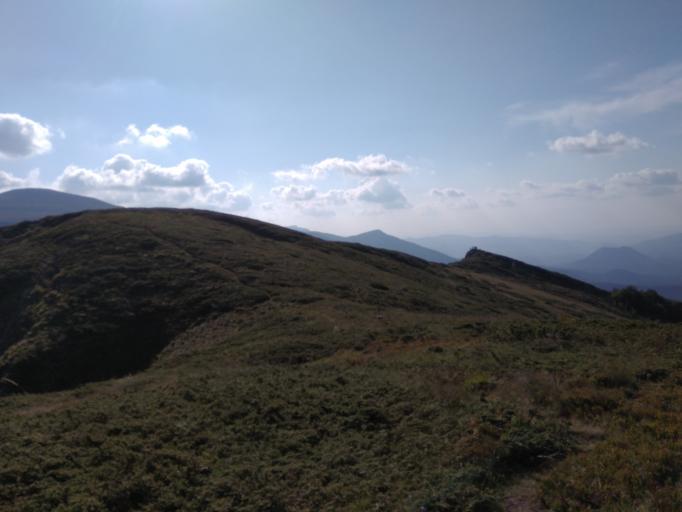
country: BG
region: Stara Zagora
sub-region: Obshtina Pavel Banya
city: Asen
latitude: 42.7609
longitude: 25.1048
